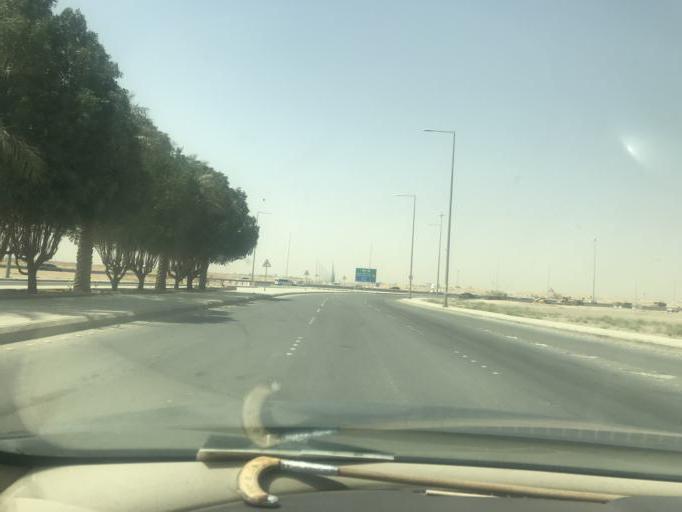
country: SA
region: Ar Riyad
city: Riyadh
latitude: 24.8074
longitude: 46.5805
